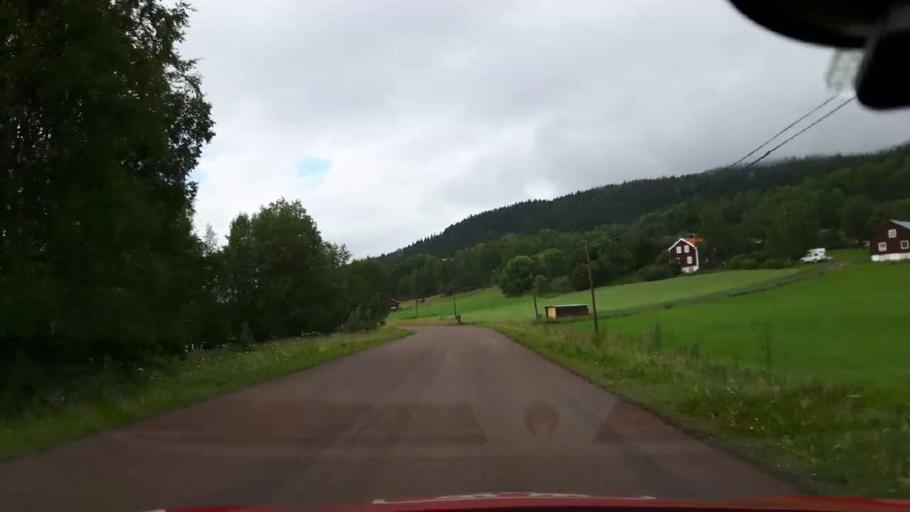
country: SE
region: Jaemtland
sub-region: Krokoms Kommun
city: Valla
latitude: 63.3810
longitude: 14.0096
